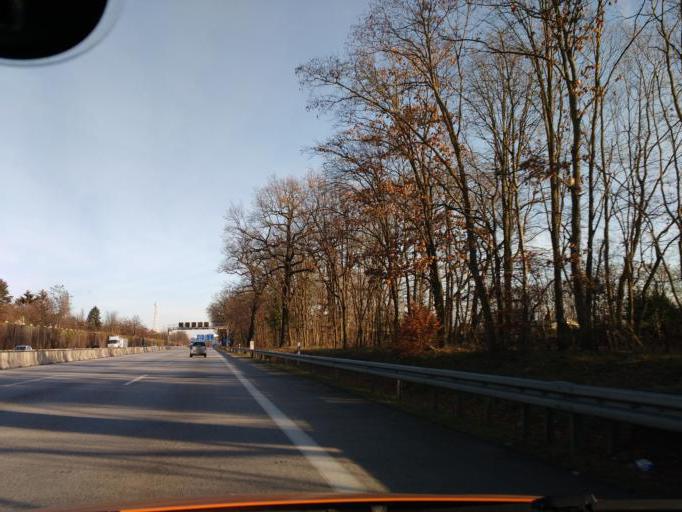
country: DE
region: Berlin
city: Grunewald
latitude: 52.4926
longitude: 13.2651
